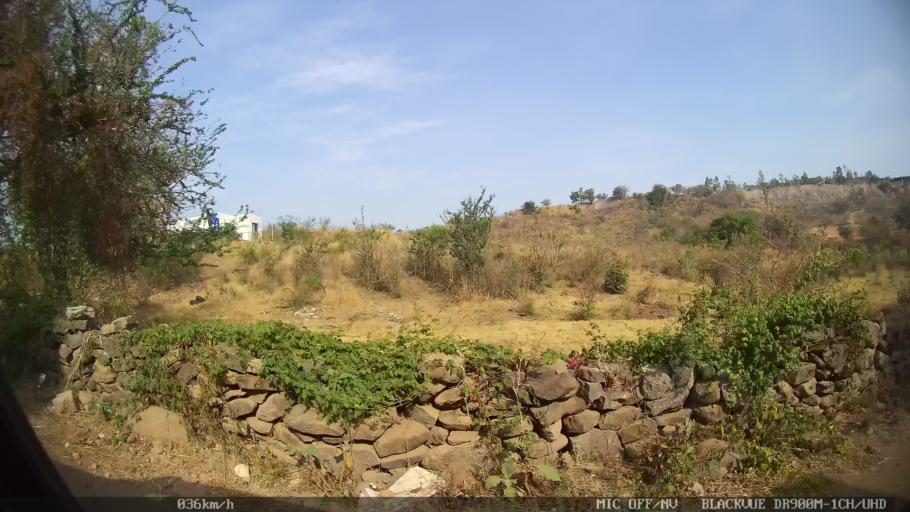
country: MX
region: Jalisco
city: Tonala
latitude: 20.6238
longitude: -103.2196
